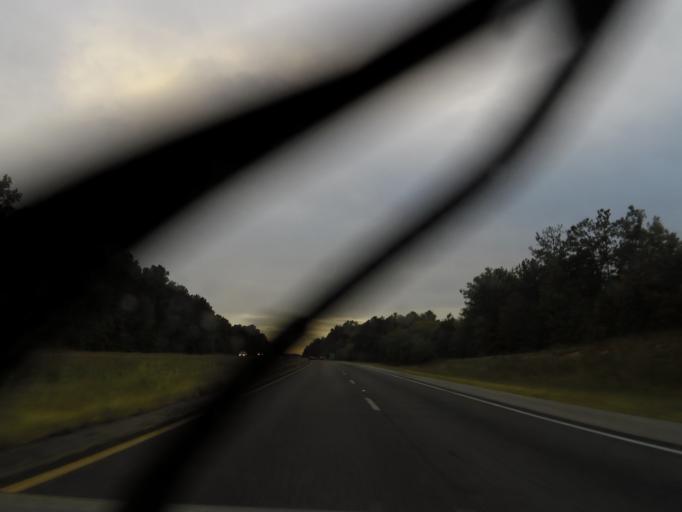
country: US
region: Alabama
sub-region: Jefferson County
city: Argo
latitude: 33.7138
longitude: -86.5185
